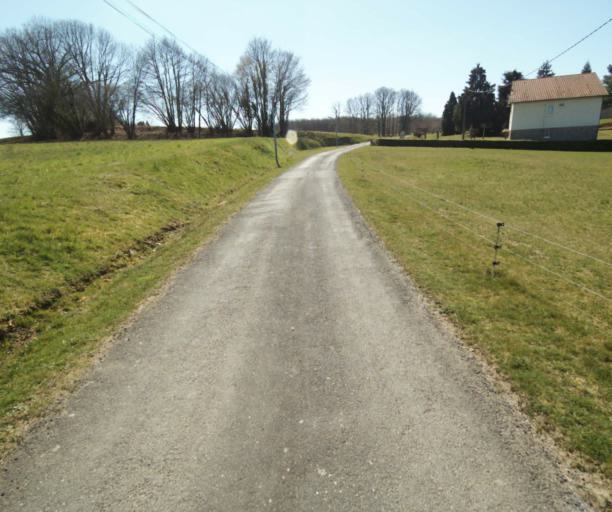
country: FR
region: Limousin
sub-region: Departement de la Correze
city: Chameyrat
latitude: 45.2723
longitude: 1.7112
